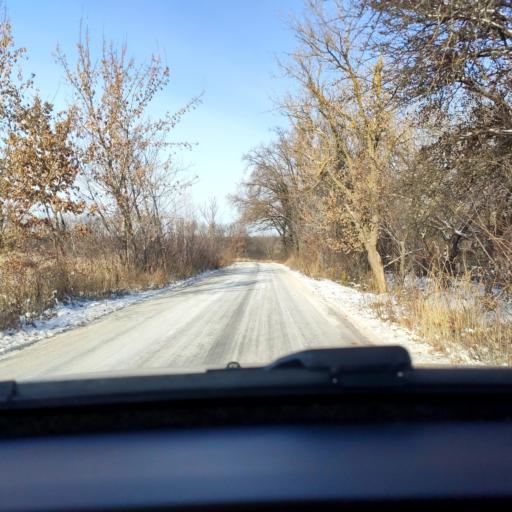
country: RU
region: Voronezj
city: Devitsa
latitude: 51.6033
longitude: 38.9885
